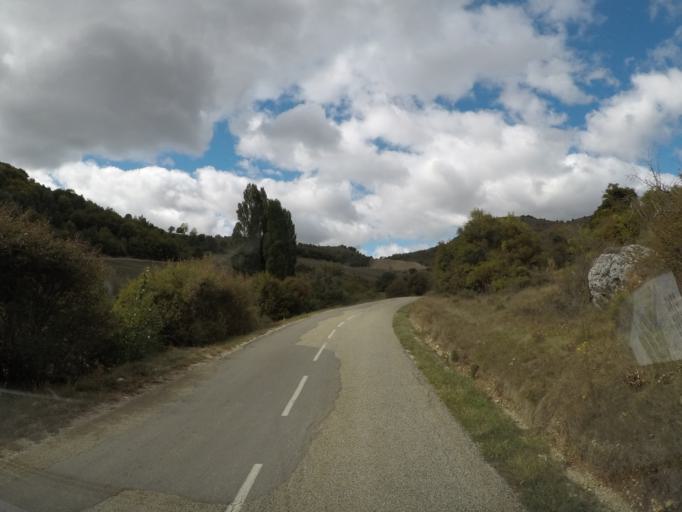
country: FR
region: Provence-Alpes-Cote d'Azur
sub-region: Departement du Vaucluse
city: Sault
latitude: 44.1838
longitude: 5.5158
